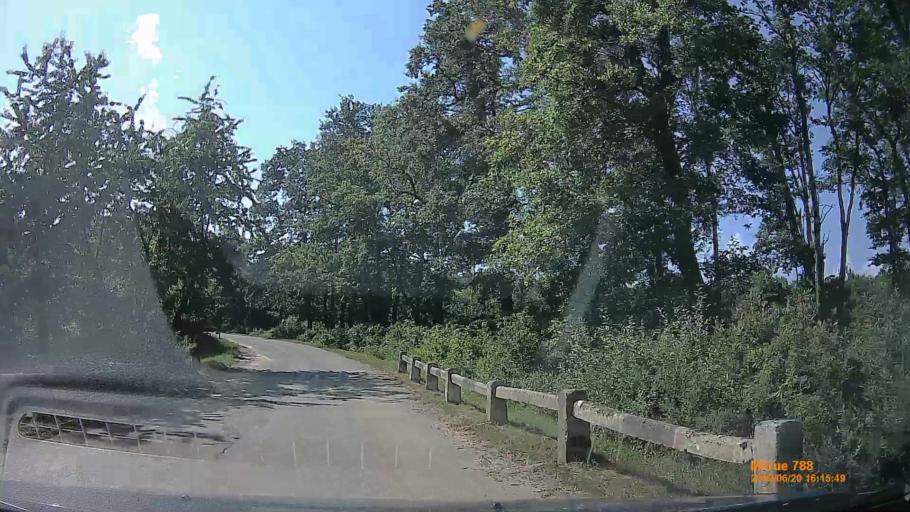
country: HU
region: Baranya
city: Buekkoesd
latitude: 46.0982
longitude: 18.0736
